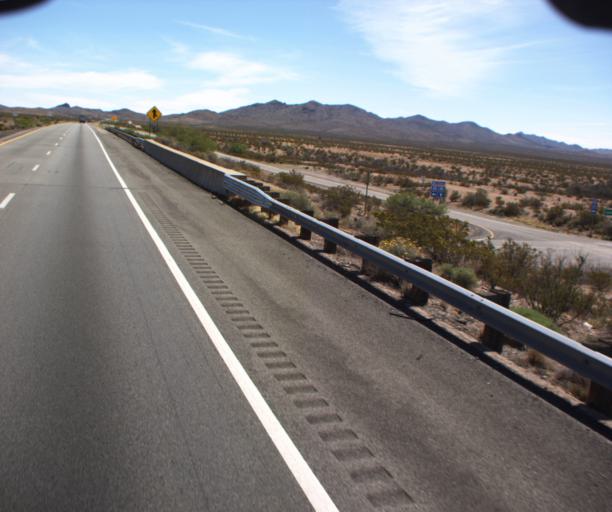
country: US
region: New Mexico
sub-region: Hidalgo County
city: Lordsburg
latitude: 32.2291
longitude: -109.0559
